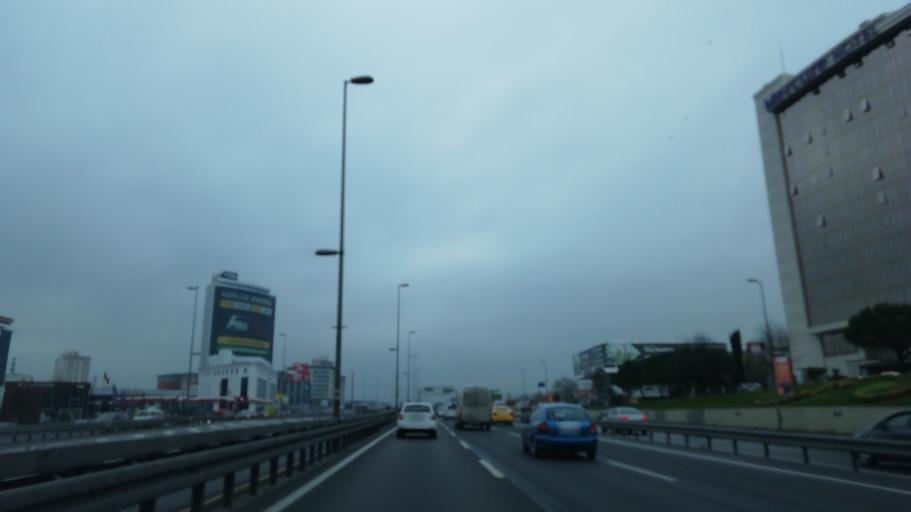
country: TR
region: Istanbul
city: Zeytinburnu
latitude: 41.0135
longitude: 28.9065
